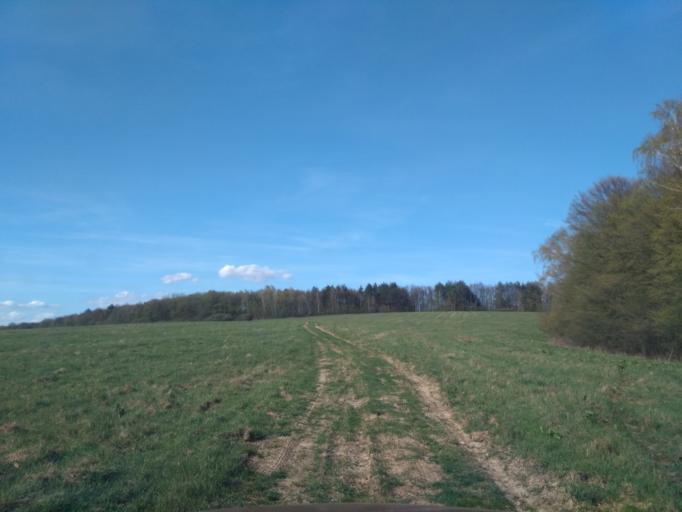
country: SK
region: Presovsky
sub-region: Okres Presov
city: Presov
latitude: 48.9202
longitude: 21.2203
